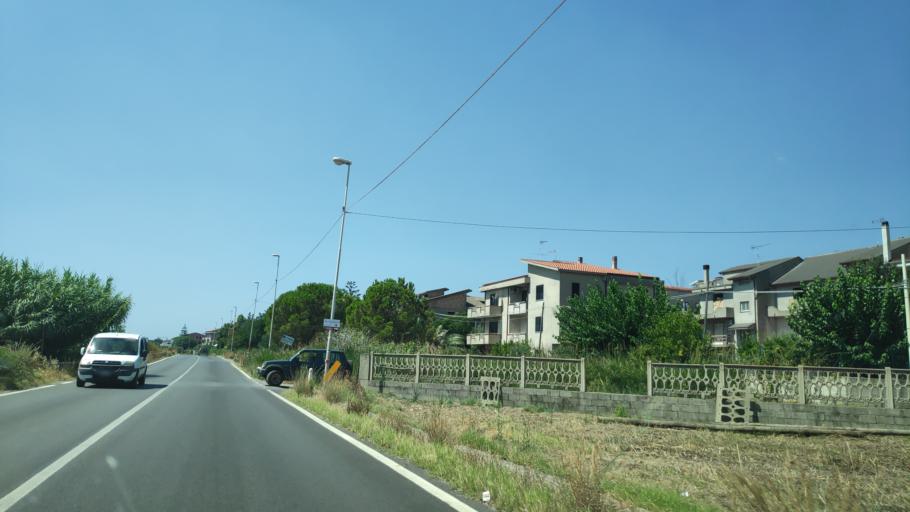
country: IT
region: Calabria
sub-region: Provincia di Reggio Calabria
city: Weather Station
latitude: 37.9539
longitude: 16.0915
